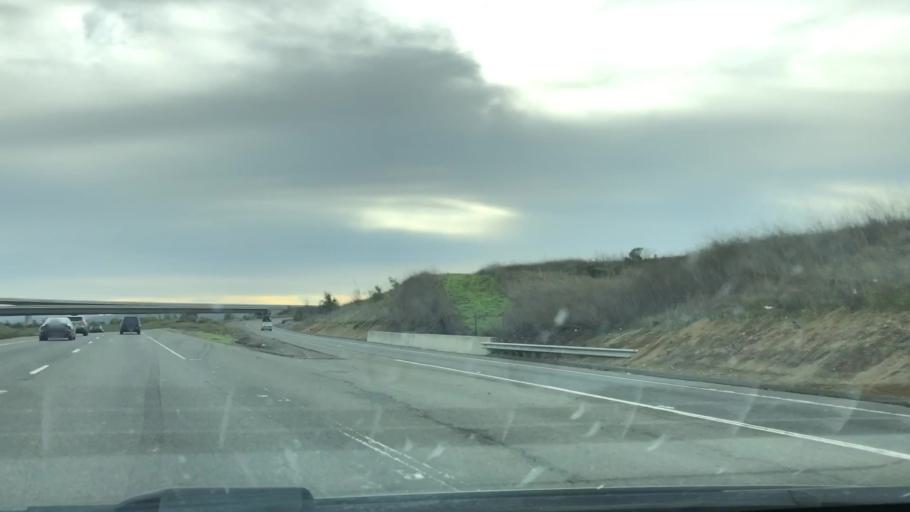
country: US
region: California
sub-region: Solano County
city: Benicia
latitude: 38.0546
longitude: -122.1301
